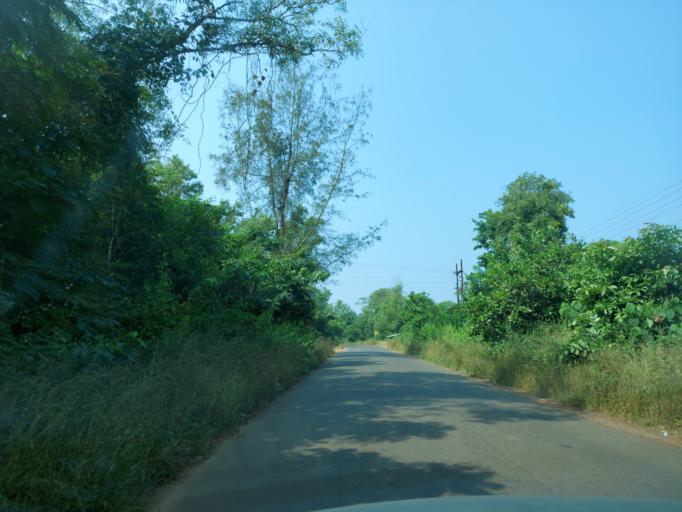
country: IN
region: Maharashtra
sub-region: Sindhudurg
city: Kudal
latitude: 15.9789
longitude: 73.6580
